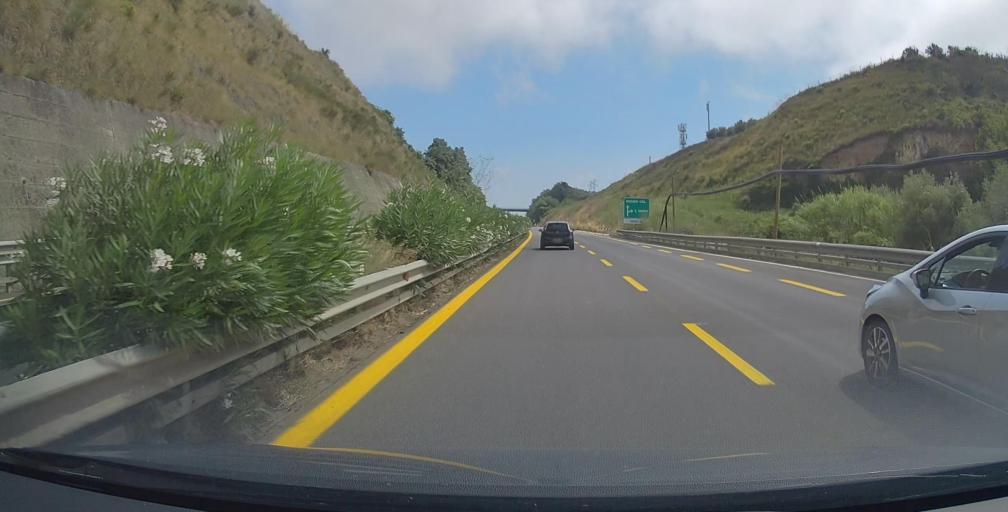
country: IT
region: Calabria
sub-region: Provincia di Vibo-Valentia
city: Sant'Onofrio
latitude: 38.7127
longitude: 16.1538
